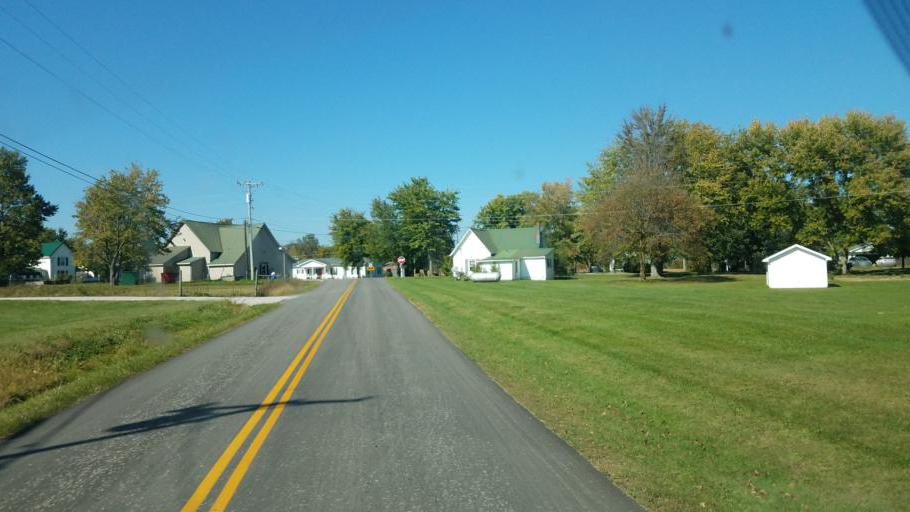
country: US
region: Kentucky
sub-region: Fleming County
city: Flemingsburg
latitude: 38.4740
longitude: -83.5919
